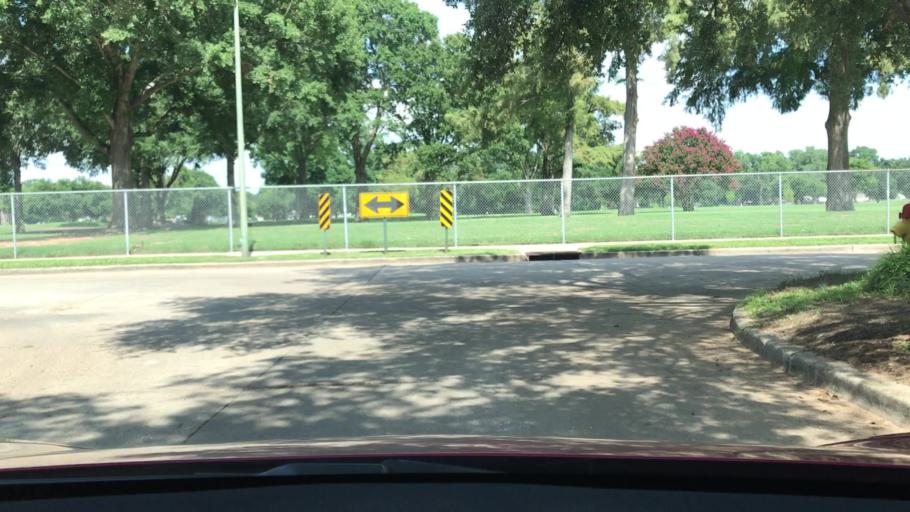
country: US
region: Louisiana
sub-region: Bossier Parish
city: Bossier City
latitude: 32.4735
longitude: -93.7288
